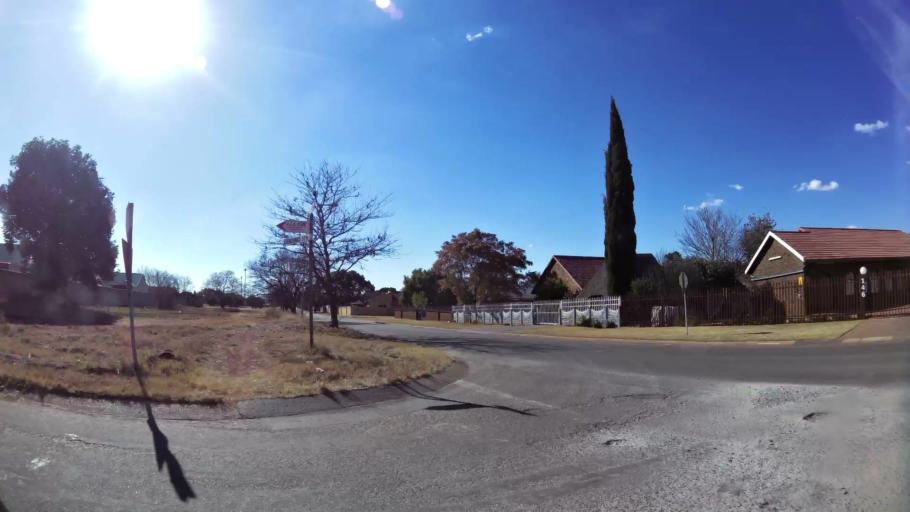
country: ZA
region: Gauteng
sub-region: West Rand District Municipality
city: Carletonville
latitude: -26.3582
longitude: 27.3746
